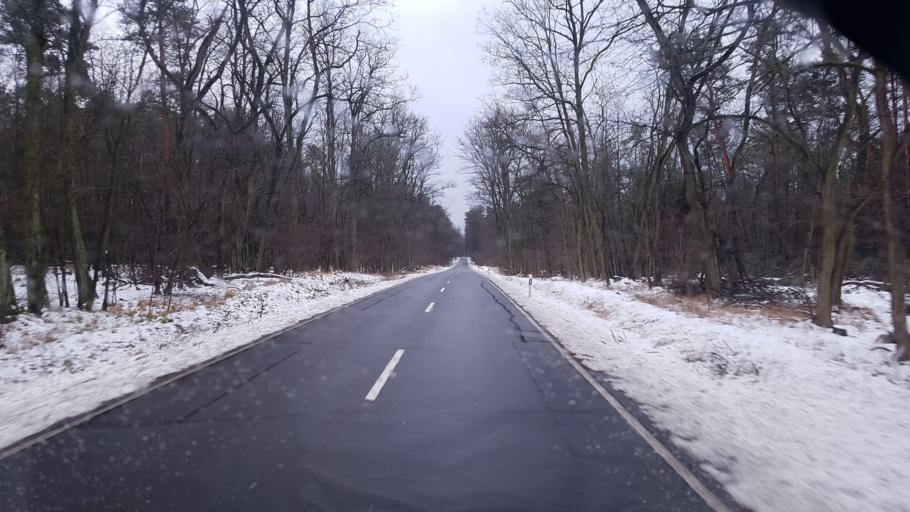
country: DE
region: Brandenburg
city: Schenkendobern
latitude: 51.9217
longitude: 14.6212
